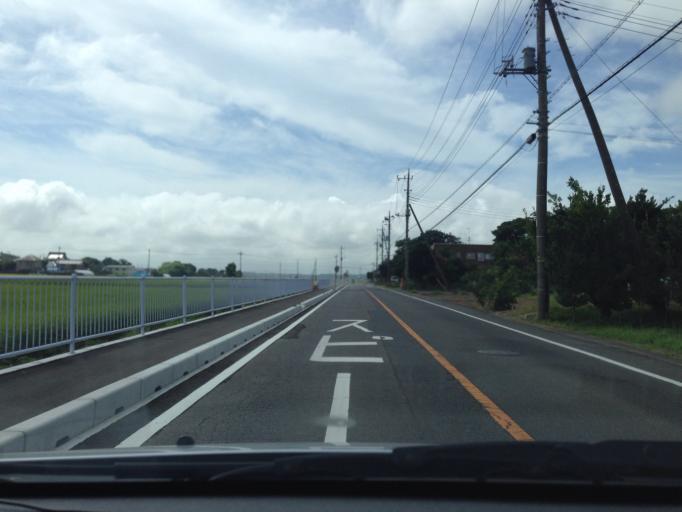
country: JP
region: Ibaraki
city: Inashiki
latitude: 36.0078
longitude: 140.3655
